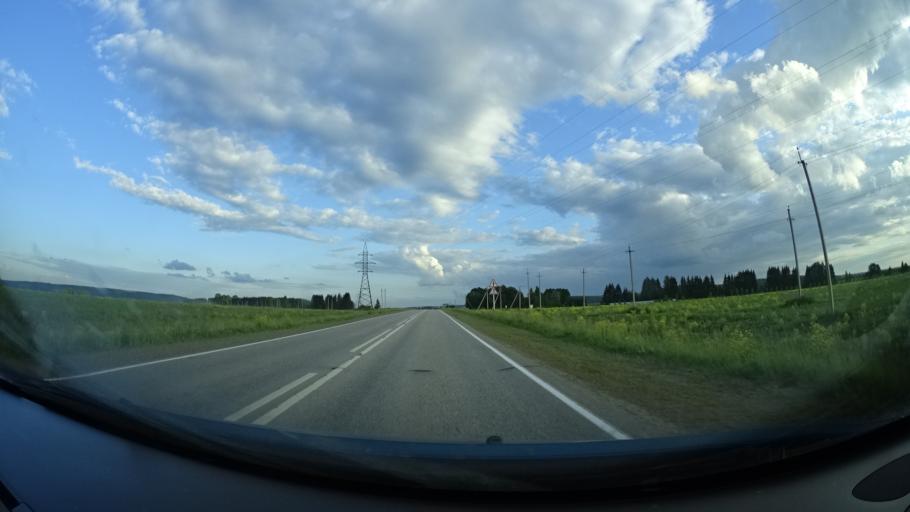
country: RU
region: Perm
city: Barda
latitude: 57.0734
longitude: 55.5426
